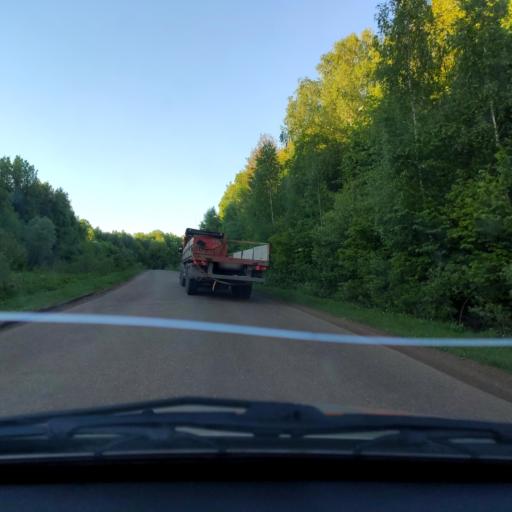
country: RU
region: Bashkortostan
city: Blagoveshchensk
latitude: 55.0324
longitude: 56.1144
